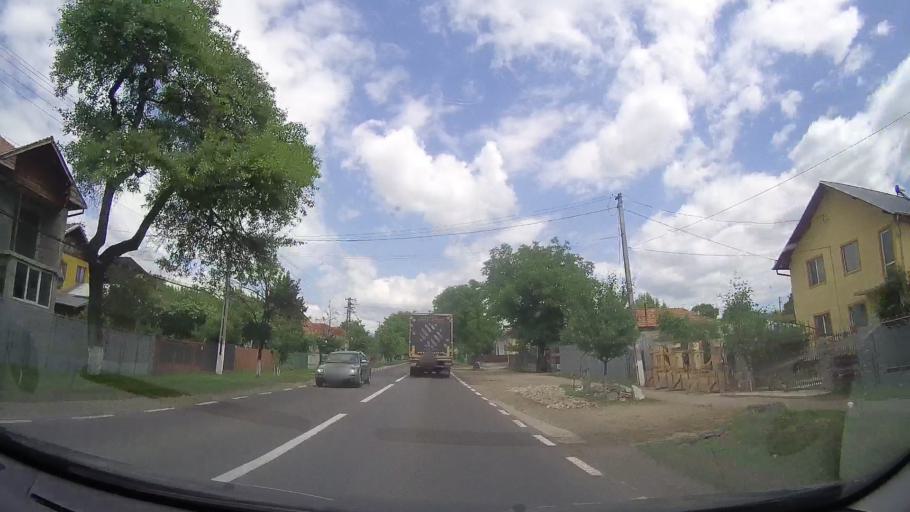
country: RO
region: Prahova
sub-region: Comuna Izvoarele
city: Homoraciu
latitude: 45.2639
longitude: 26.0146
